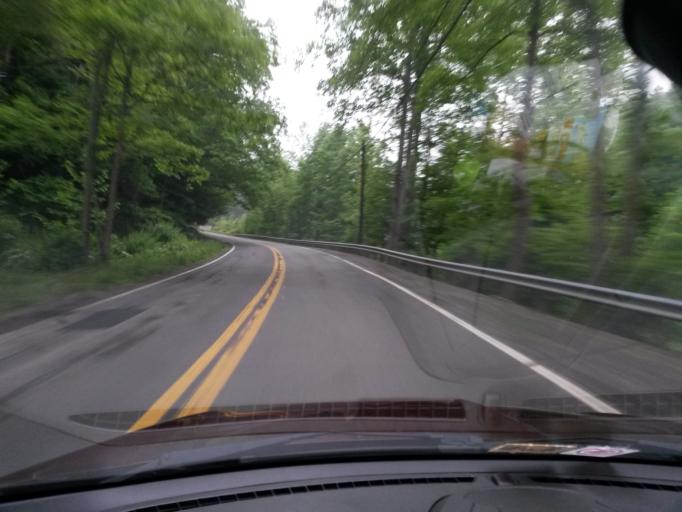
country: US
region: West Virginia
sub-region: Wyoming County
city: Pineville
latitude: 37.5226
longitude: -81.5900
